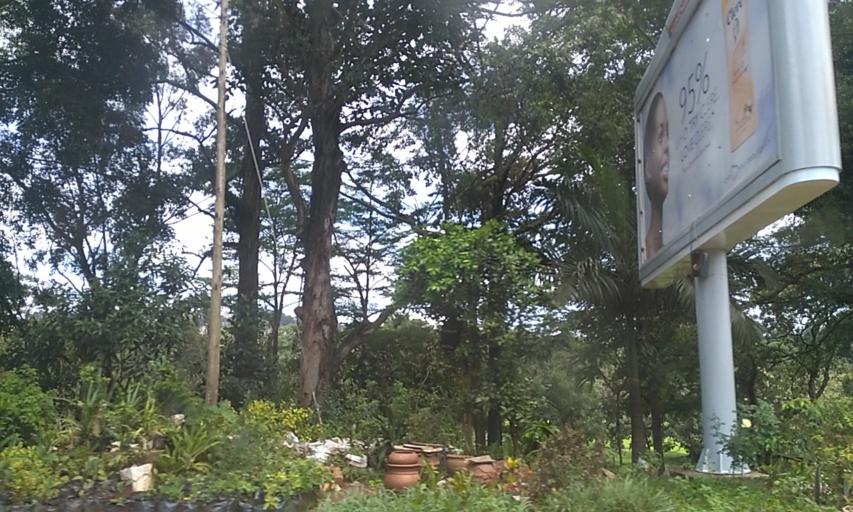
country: UG
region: Central Region
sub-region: Kampala District
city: Kampala
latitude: 0.3213
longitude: 32.5889
